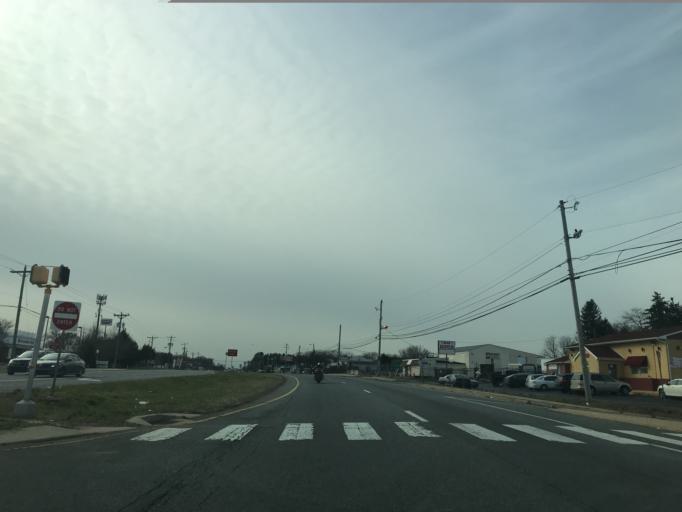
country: US
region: Delaware
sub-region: New Castle County
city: Bear
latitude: 39.6475
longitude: -75.6341
